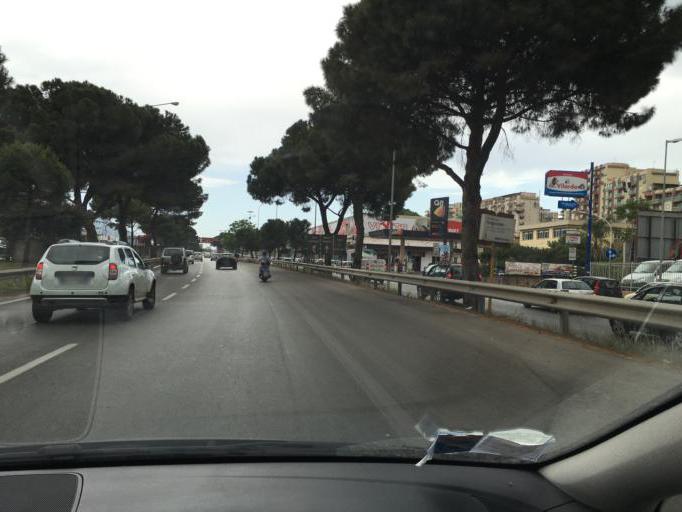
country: IT
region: Sicily
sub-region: Palermo
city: Palermo
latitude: 38.1440
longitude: 13.3306
